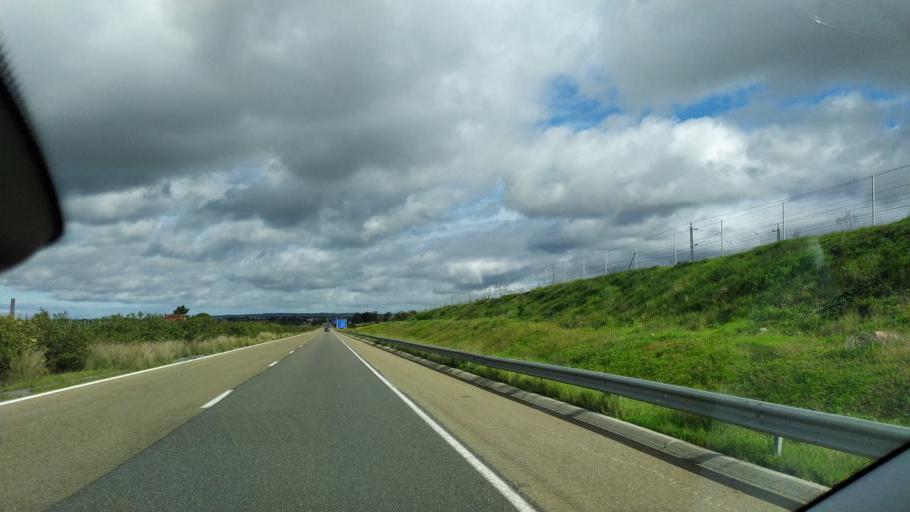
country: MA
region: Gharb-Chrarda-Beni Hssen
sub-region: Kenitra Province
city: Lalla Mimouna
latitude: 34.8462
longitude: -6.2252
